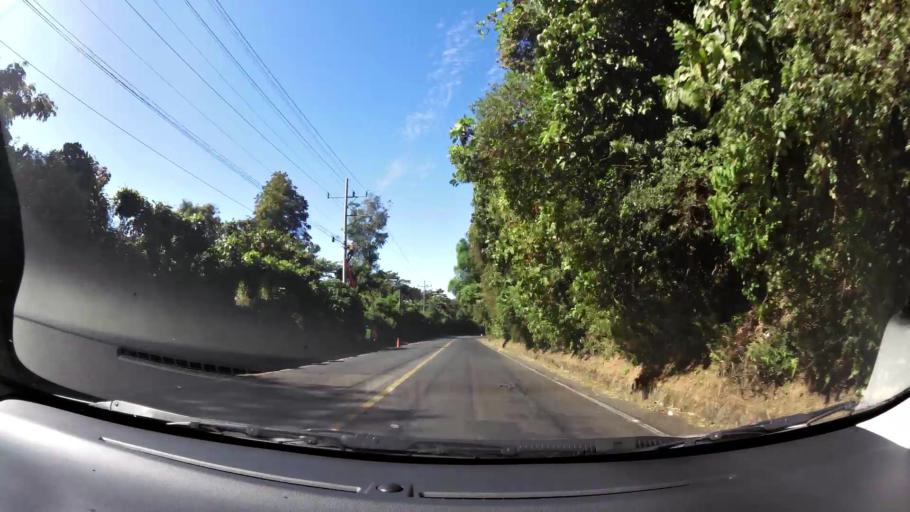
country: SV
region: Ahuachapan
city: Concepcion de Ataco
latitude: 13.8497
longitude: -89.8159
